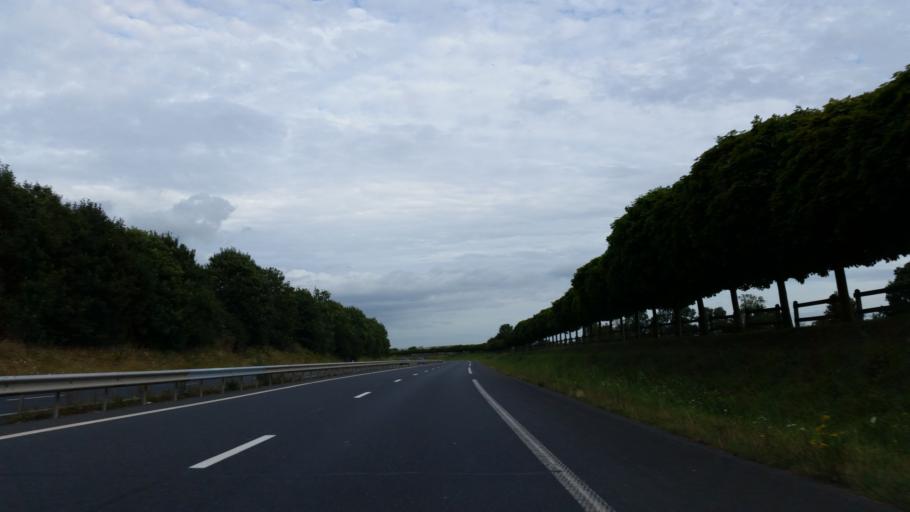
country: FR
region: Lower Normandy
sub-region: Departement du Calvados
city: Grandcamp-Maisy
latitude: 49.3416
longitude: -1.0177
